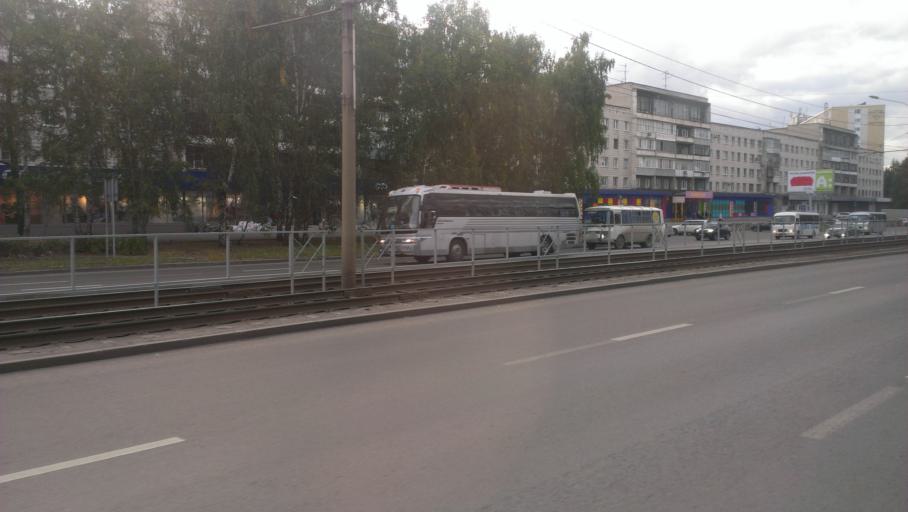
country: RU
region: Altai Krai
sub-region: Gorod Barnaulskiy
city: Barnaul
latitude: 53.3457
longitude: 83.7654
